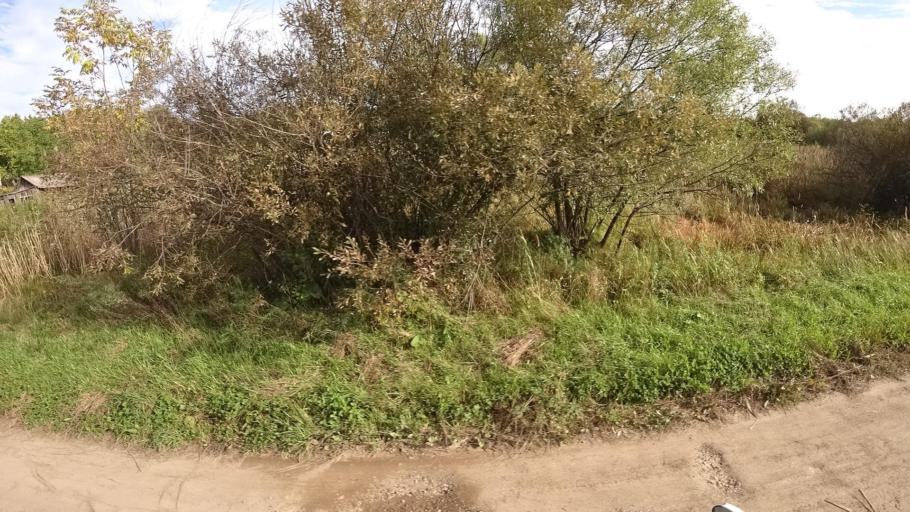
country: RU
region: Primorskiy
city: Dostoyevka
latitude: 44.3080
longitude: 133.4644
